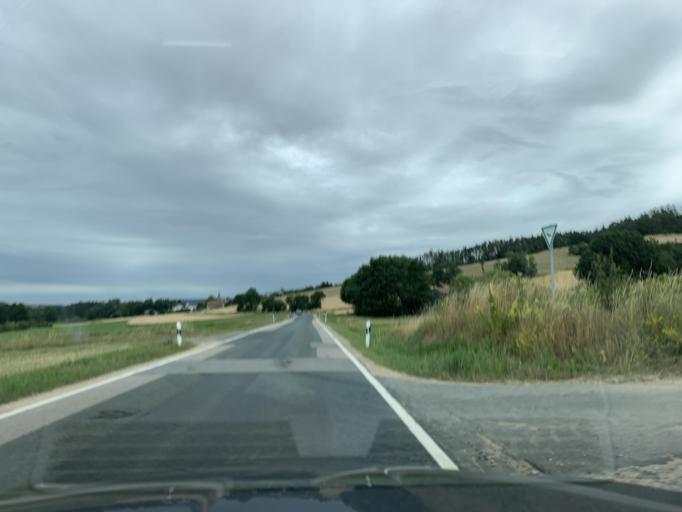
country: DE
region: Bavaria
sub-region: Upper Palatinate
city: Schwarzhofen
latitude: 49.3691
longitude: 12.3512
